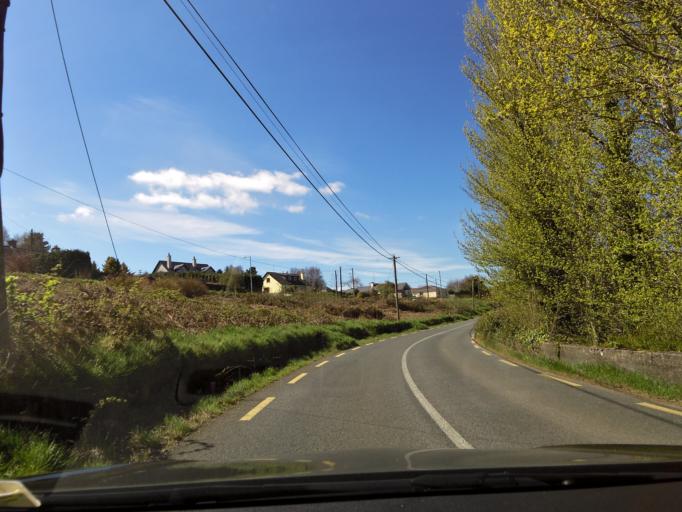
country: IE
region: Leinster
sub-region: Wicklow
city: Aughrim
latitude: 52.8517
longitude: -6.3146
